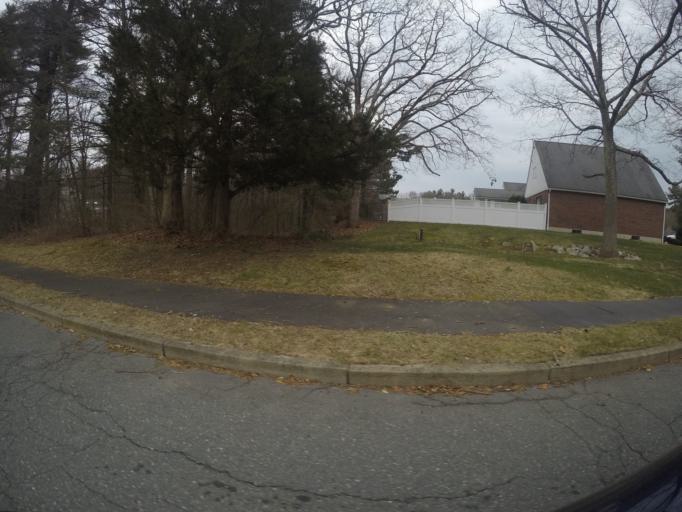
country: US
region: Massachusetts
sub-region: Norfolk County
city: Stoughton
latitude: 42.0782
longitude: -71.1037
